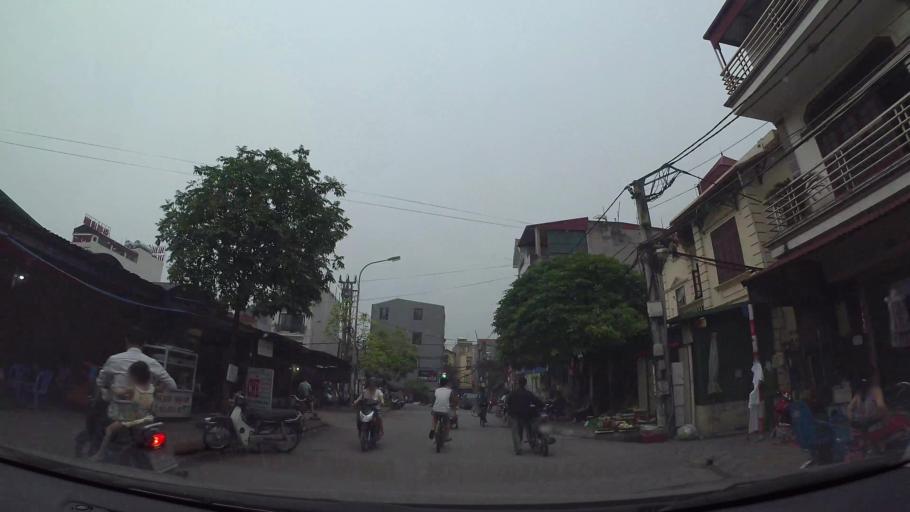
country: VN
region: Ha Noi
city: Trau Quy
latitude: 21.0401
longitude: 105.9026
